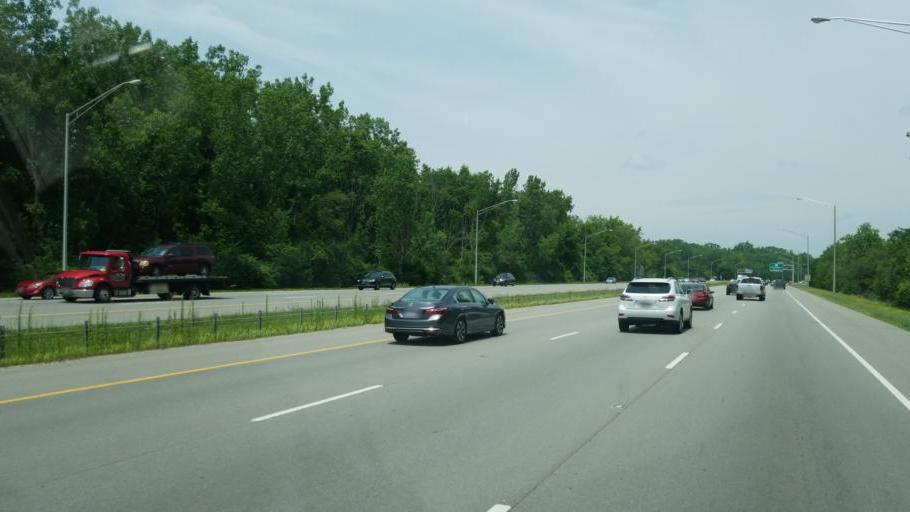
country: US
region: Ohio
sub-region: Franklin County
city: Worthington
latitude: 40.0692
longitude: -83.0339
